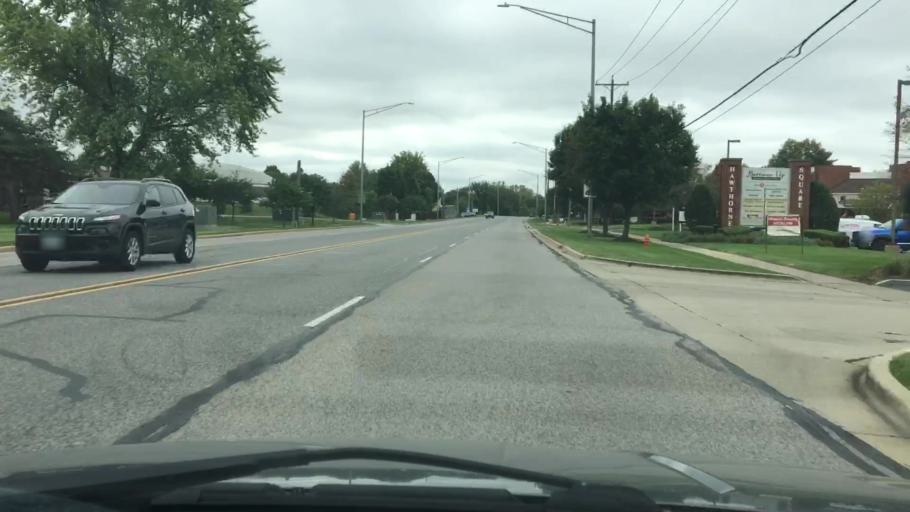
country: US
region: Illinois
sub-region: DuPage County
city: Naperville
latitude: 41.7362
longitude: -88.1283
